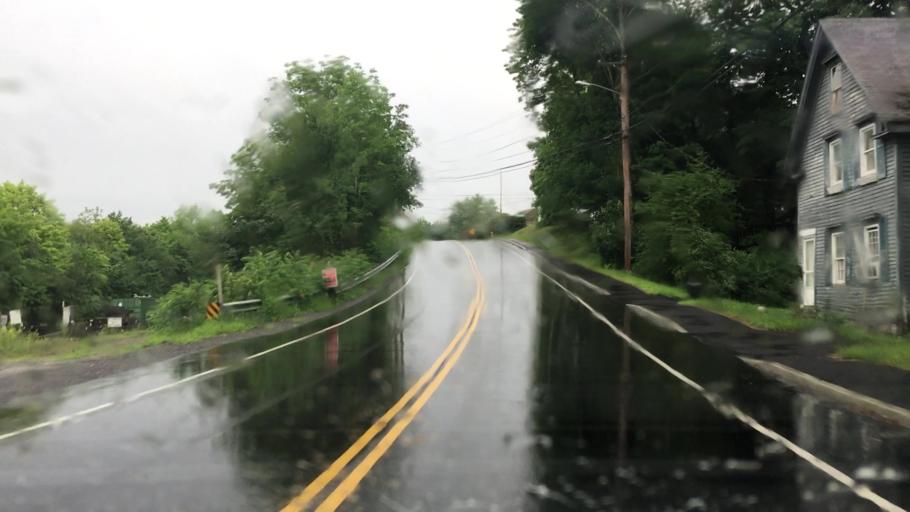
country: US
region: Maine
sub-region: Kennebec County
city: Randolph
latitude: 44.2268
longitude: -69.7685
